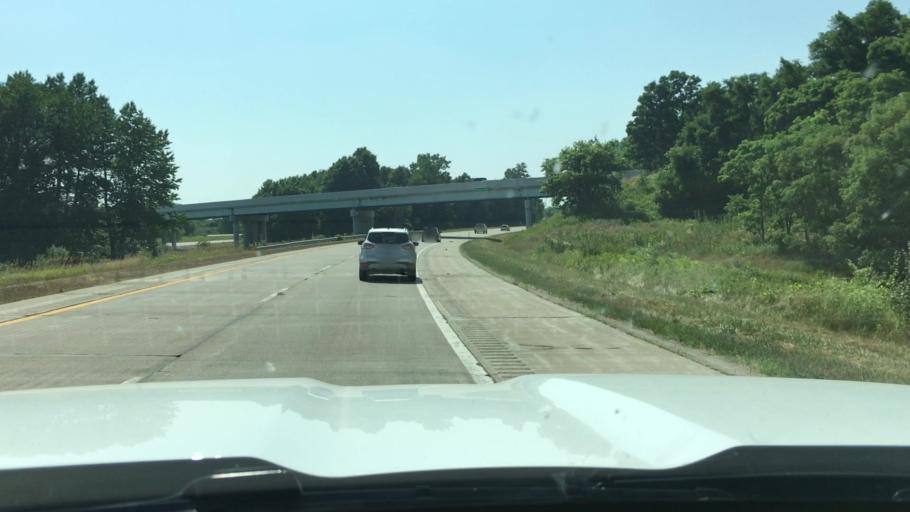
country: US
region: Michigan
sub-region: Clinton County
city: Wacousta
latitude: 42.7885
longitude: -84.6623
